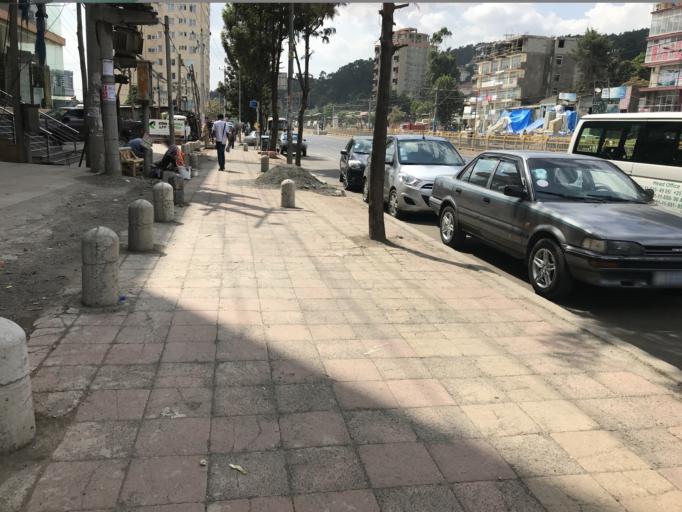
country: ET
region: Adis Abeba
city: Addis Ababa
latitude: 9.0198
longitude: 38.8115
